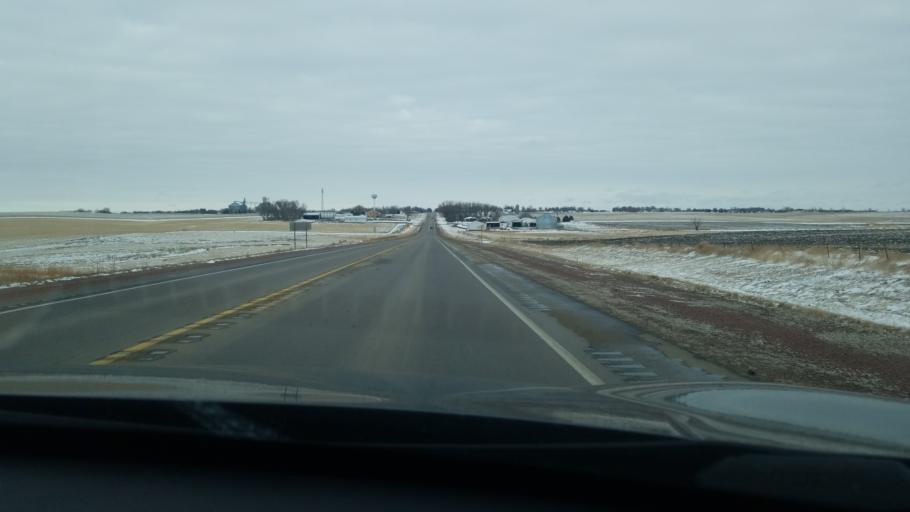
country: US
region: South Dakota
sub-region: Lincoln County
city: Canton
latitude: 43.4337
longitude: -96.4290
